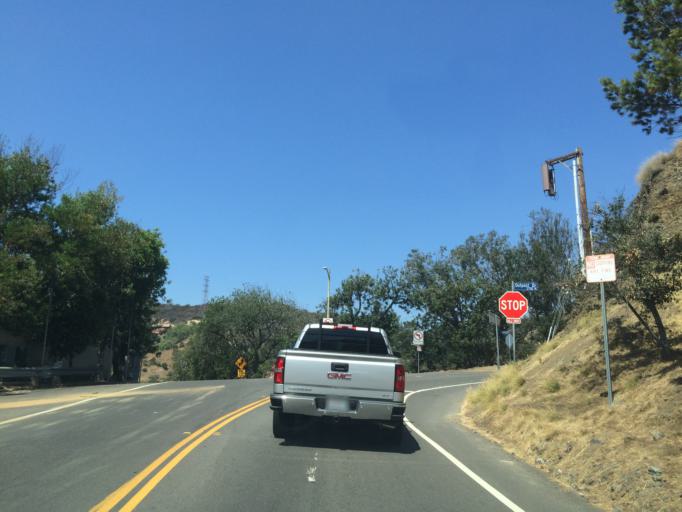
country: US
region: California
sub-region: Los Angeles County
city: Universal City
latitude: 34.1182
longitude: -118.3466
